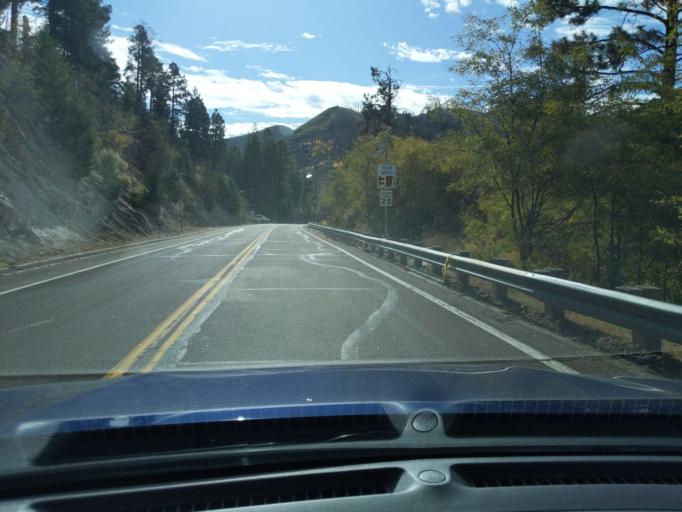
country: US
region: Arizona
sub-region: Pinal County
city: Oracle
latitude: 32.4474
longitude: -110.7568
